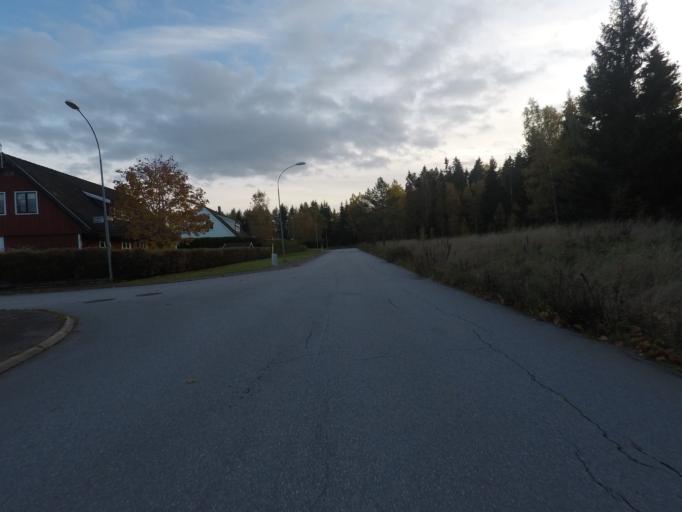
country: SE
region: OErebro
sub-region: Karlskoga Kommun
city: Karlskoga
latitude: 59.3089
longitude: 14.4697
